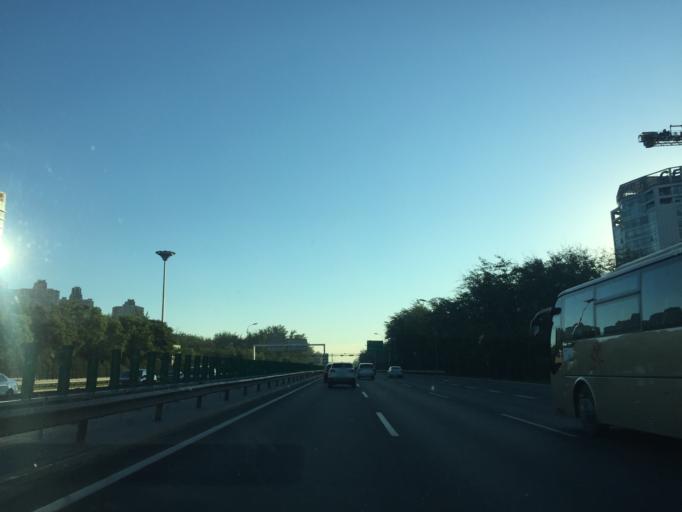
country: CN
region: Beijing
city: Wangjing
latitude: 39.9591
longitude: 116.4513
